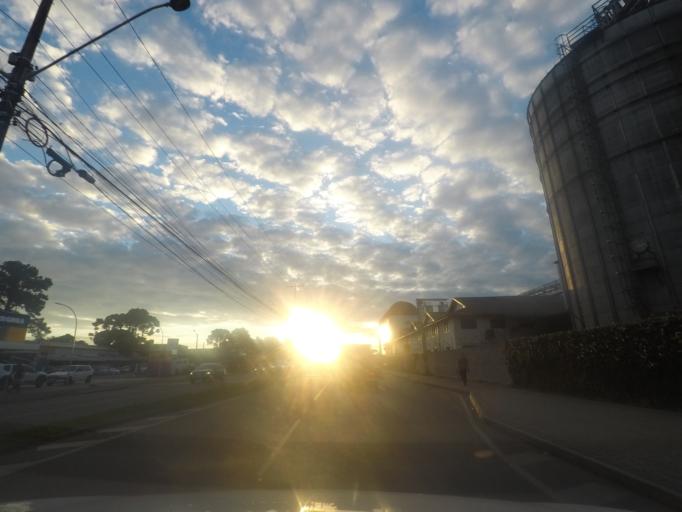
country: BR
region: Parana
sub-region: Pinhais
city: Pinhais
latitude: -25.4474
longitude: -49.1881
